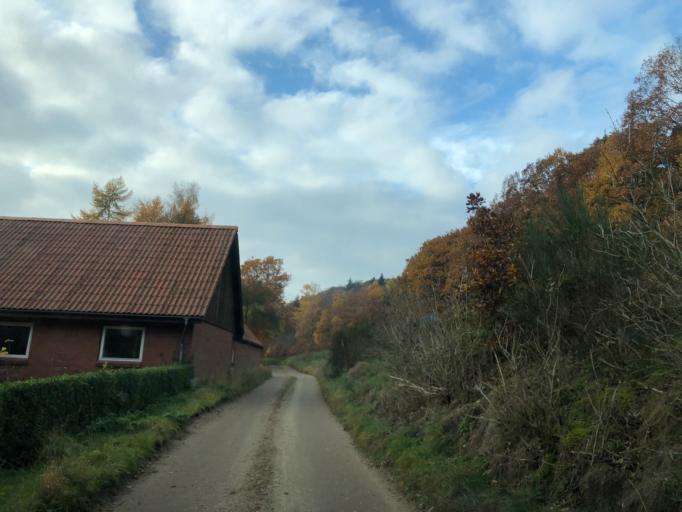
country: DK
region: Central Jutland
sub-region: Silkeborg Kommune
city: Silkeborg
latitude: 56.1450
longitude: 9.4856
